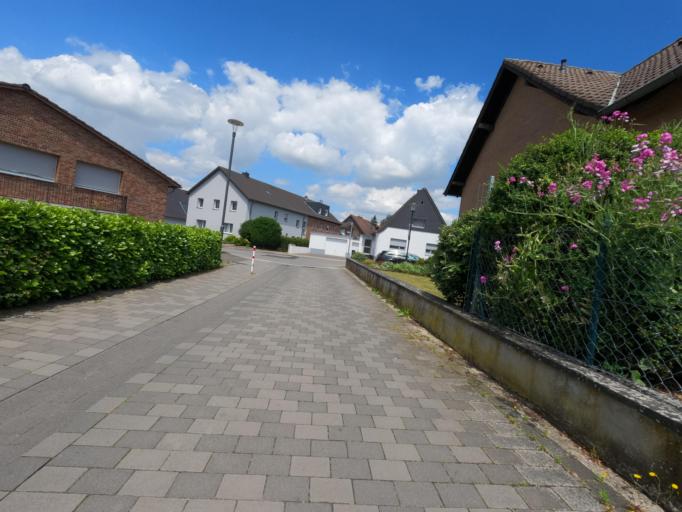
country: DE
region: North Rhine-Westphalia
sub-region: Regierungsbezirk Koln
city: Ubach-Palenberg
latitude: 50.9150
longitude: 6.1184
